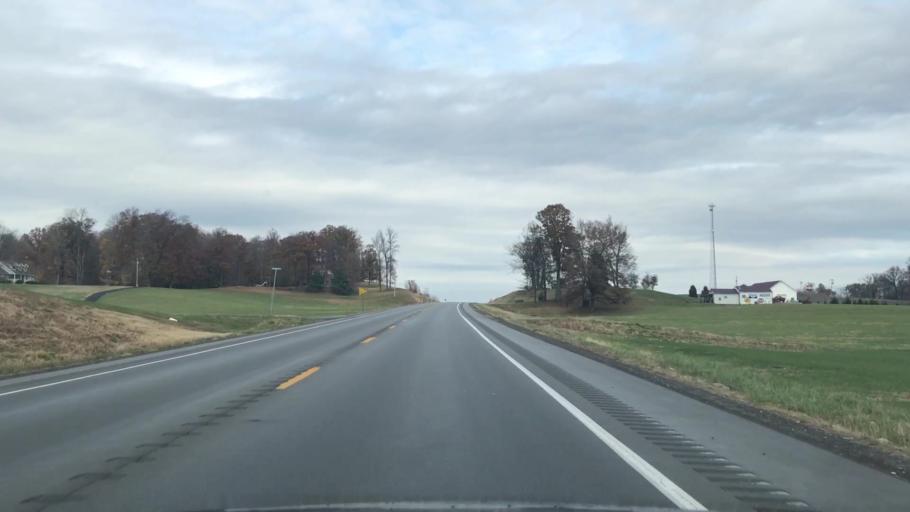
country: US
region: Kentucky
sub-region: Monroe County
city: Tompkinsville
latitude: 36.7853
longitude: -85.6862
